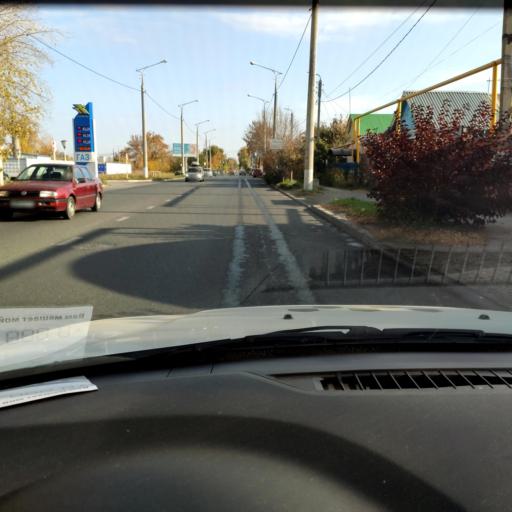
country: RU
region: Samara
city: Tol'yatti
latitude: 53.5093
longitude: 49.3926
